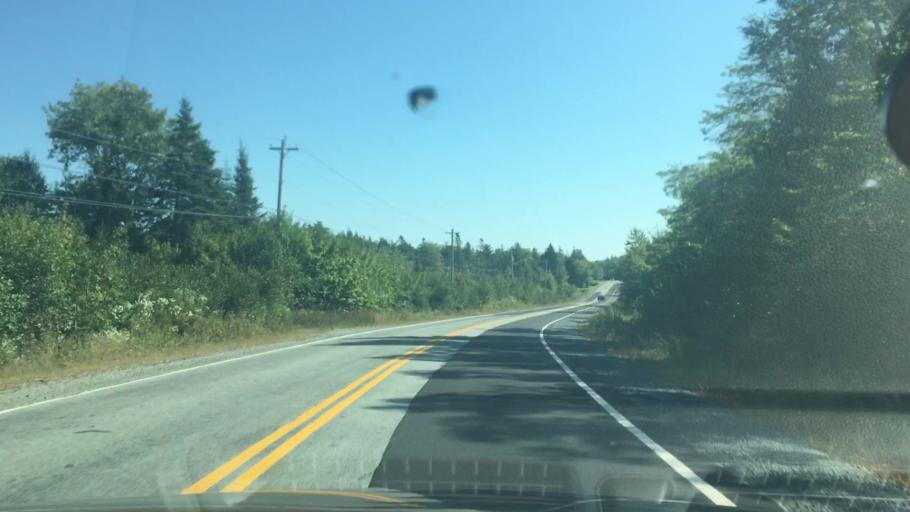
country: CA
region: Nova Scotia
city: New Glasgow
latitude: 44.9103
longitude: -62.5512
